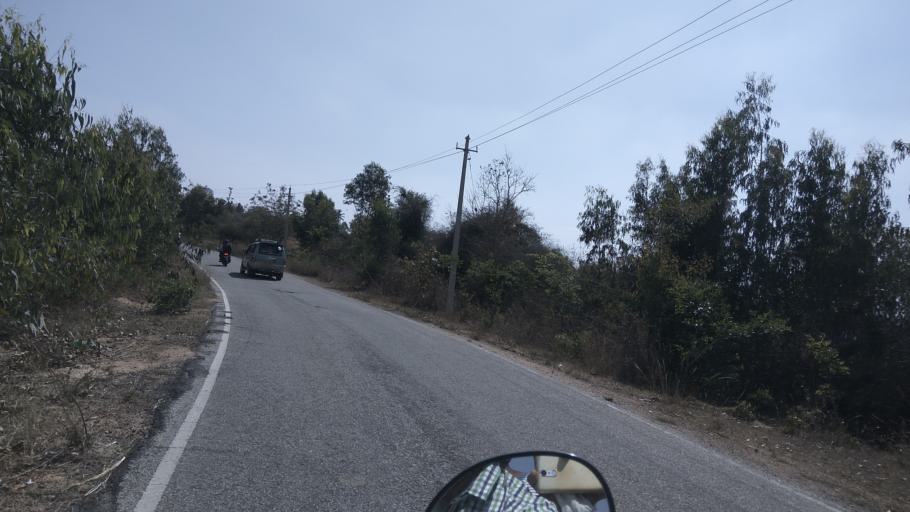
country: IN
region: Karnataka
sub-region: Kolar
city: Mulbagal
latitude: 13.1996
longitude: 78.3553
